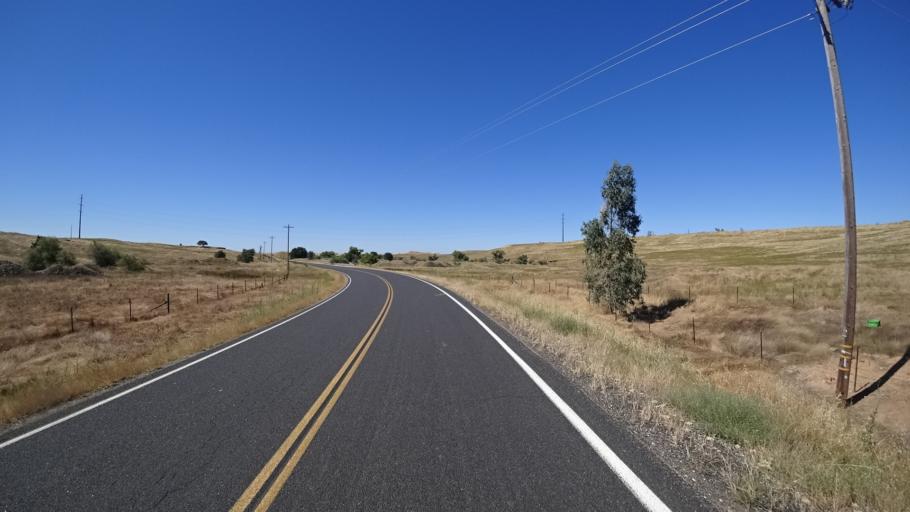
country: US
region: California
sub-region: Calaveras County
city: Rancho Calaveras
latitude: 38.0642
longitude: -120.8710
